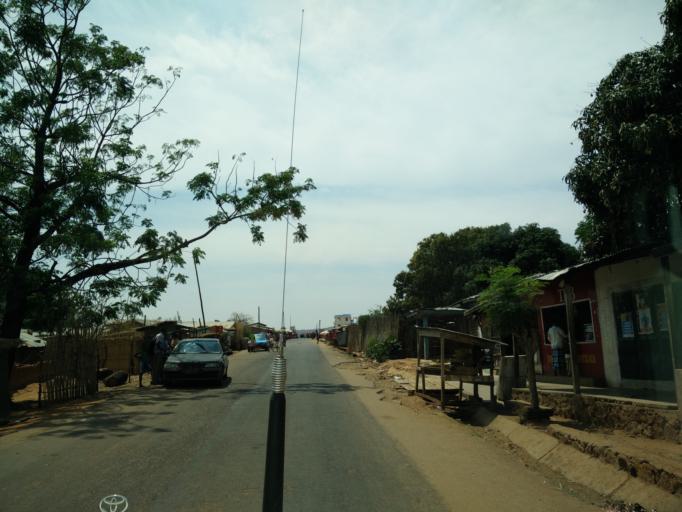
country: MG
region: Ihorombe
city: Ranohira
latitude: -22.7718
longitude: 45.1056
